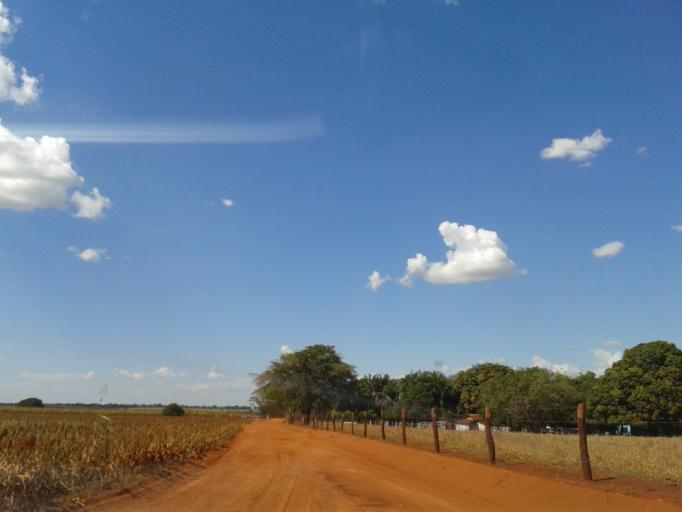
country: BR
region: Minas Gerais
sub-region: Capinopolis
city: Capinopolis
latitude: -18.6012
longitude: -49.5080
